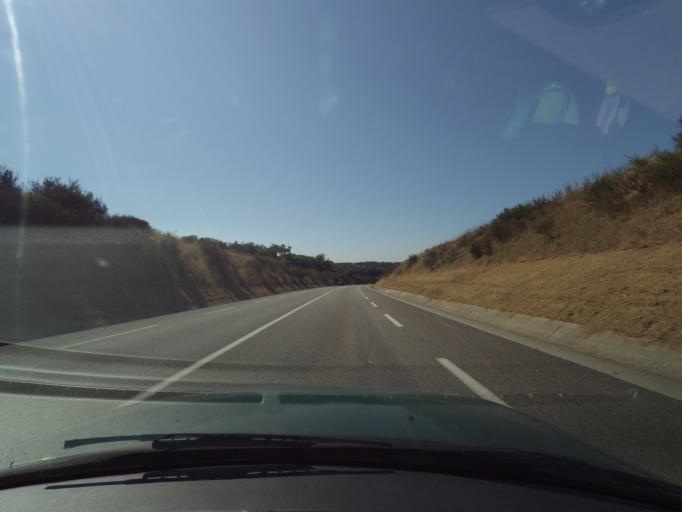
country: FR
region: Limousin
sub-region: Departement de la Haute-Vienne
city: Bellac
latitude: 46.1223
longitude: 1.0752
